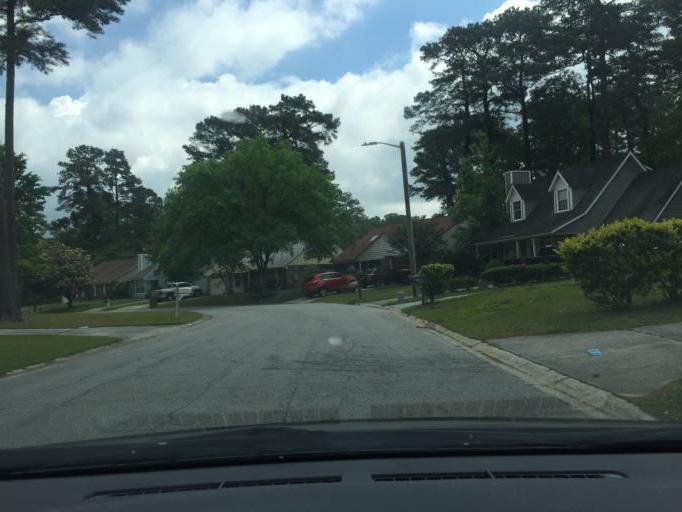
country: US
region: Georgia
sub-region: Chatham County
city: Montgomery
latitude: 31.9963
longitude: -81.1393
